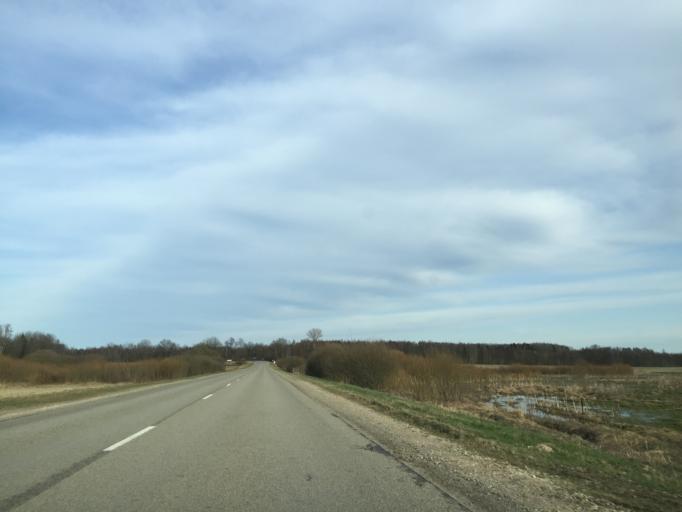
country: LV
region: Lielvarde
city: Lielvarde
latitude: 56.7986
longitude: 24.8370
